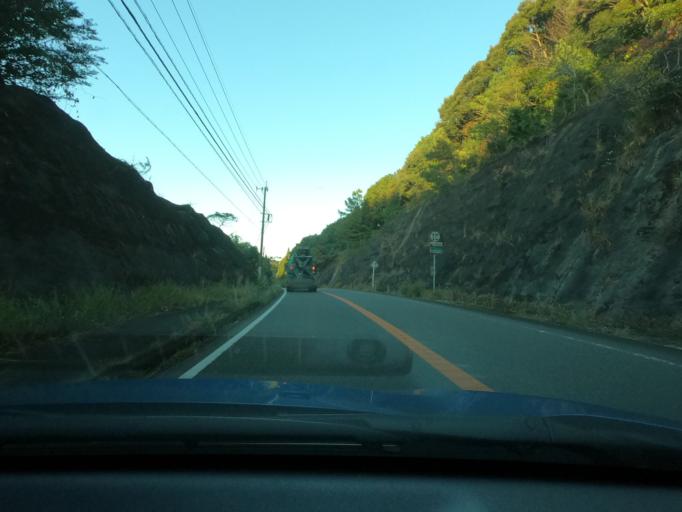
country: JP
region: Kagoshima
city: Satsumasendai
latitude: 31.8075
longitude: 130.3685
